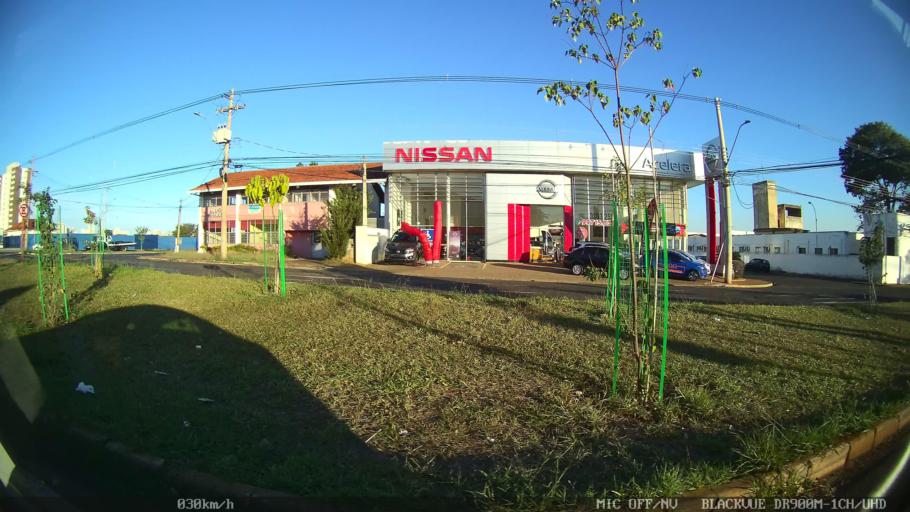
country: BR
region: Sao Paulo
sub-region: Araraquara
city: Araraquara
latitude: -21.7855
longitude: -48.2032
